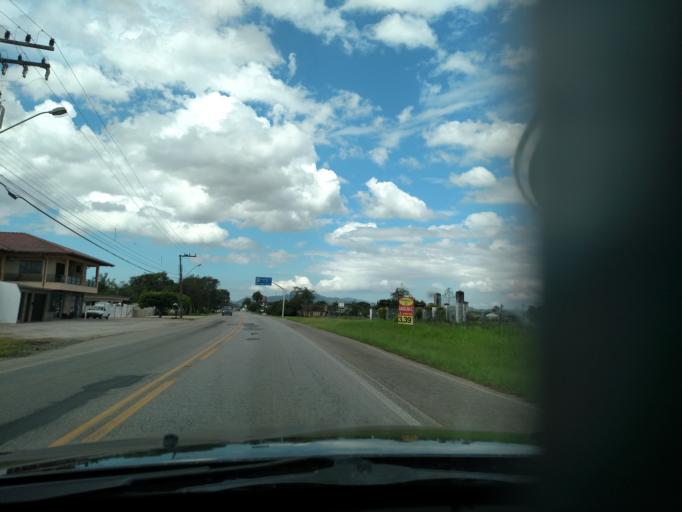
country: BR
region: Santa Catarina
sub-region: Gaspar
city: Gaspar
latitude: -26.9110
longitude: -48.9259
